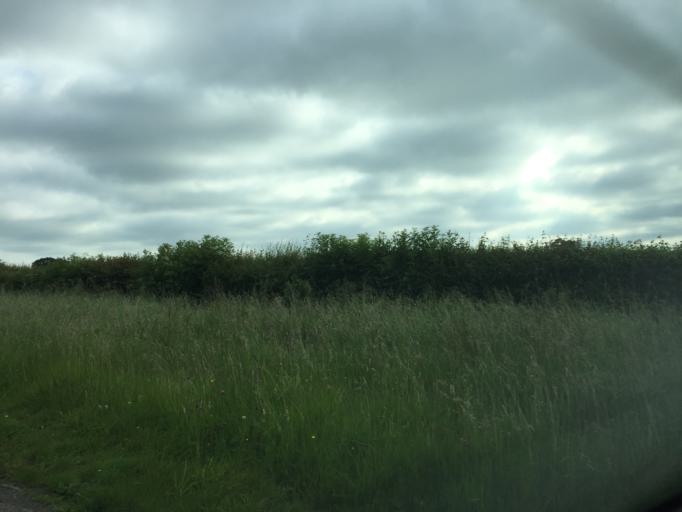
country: GB
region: England
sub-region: South Gloucestershire
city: Horton
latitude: 51.5675
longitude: -2.3556
